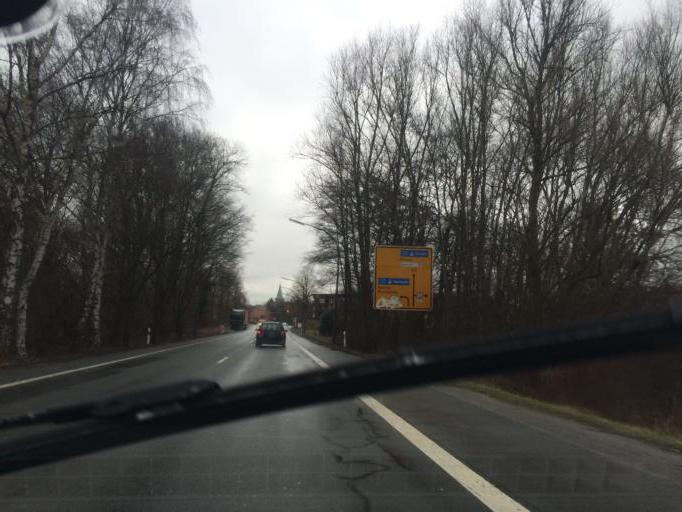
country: DE
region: North Rhine-Westphalia
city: Dorsten
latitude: 51.6536
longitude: 6.9665
